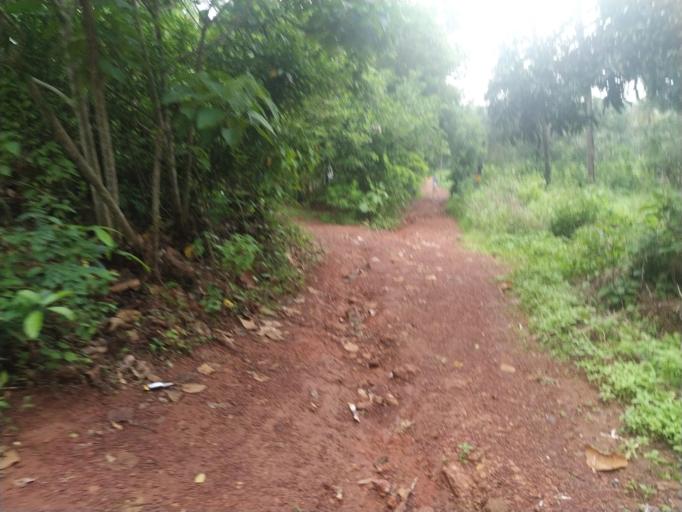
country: IN
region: Kerala
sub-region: Kasaragod District
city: Kannangad
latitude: 12.4029
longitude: 75.0586
